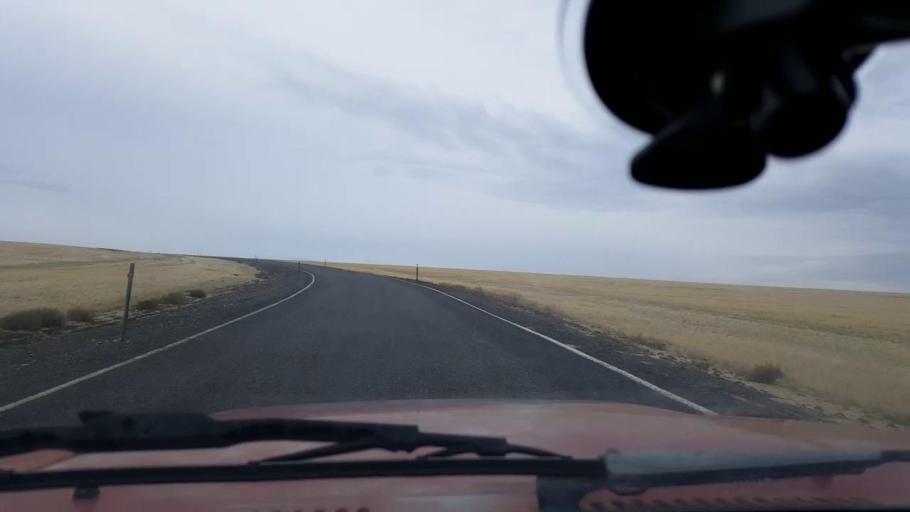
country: US
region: Washington
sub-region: Asotin County
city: Clarkston Heights-Vineland
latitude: 46.3454
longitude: -117.2595
